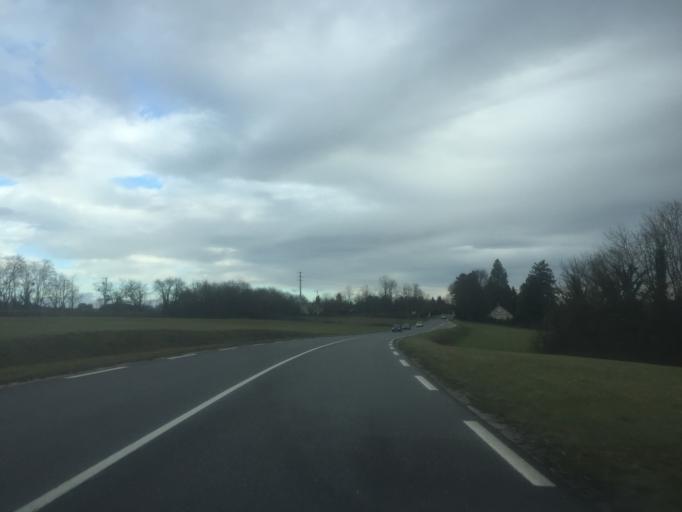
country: FR
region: Franche-Comte
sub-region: Departement du Doubs
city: Saint-Vit
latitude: 47.1743
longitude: 5.7846
